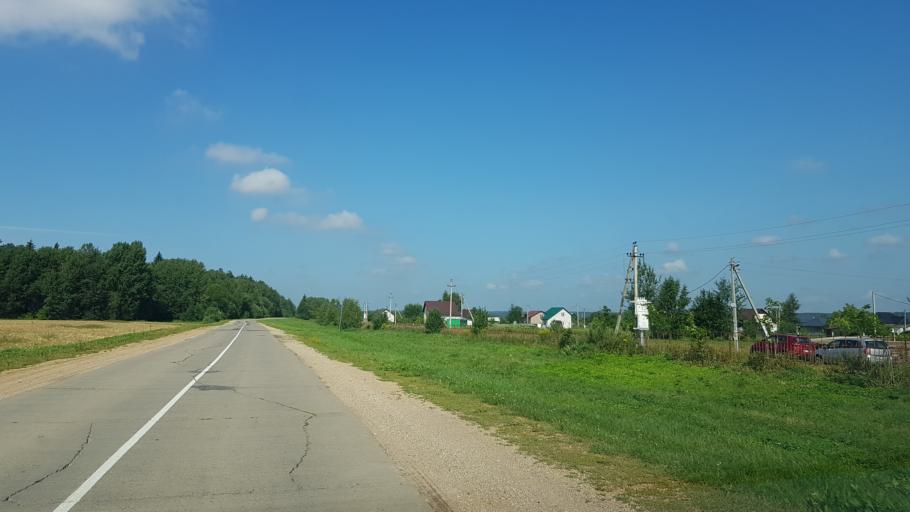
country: BY
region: Minsk
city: Dzyarzhynsk
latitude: 53.7099
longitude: 27.0739
